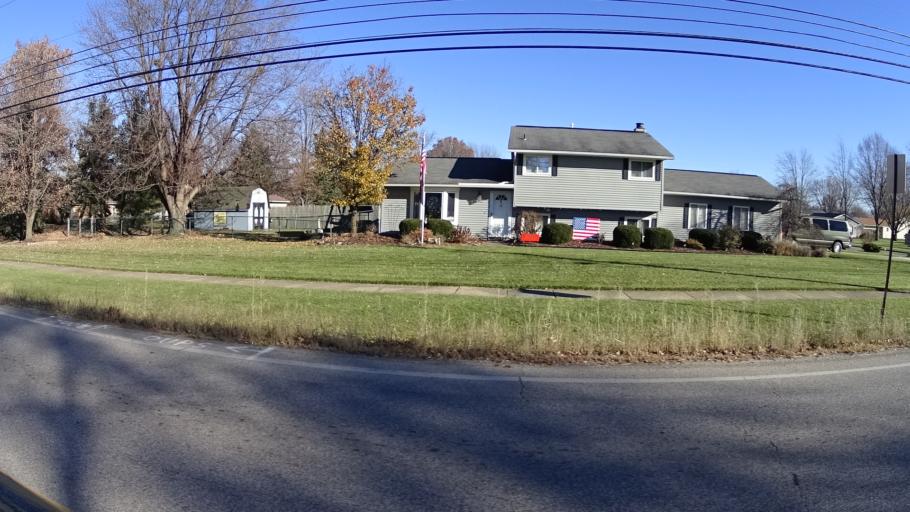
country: US
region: Ohio
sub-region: Lorain County
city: North Ridgeville
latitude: 41.4171
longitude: -82.0187
